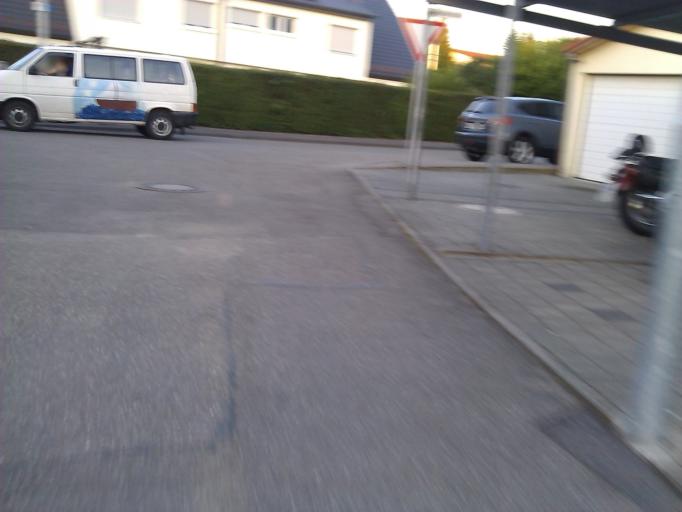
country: DE
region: Baden-Wuerttemberg
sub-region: Regierungsbezirk Stuttgart
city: Heilbronn
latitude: 49.1391
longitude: 9.1702
